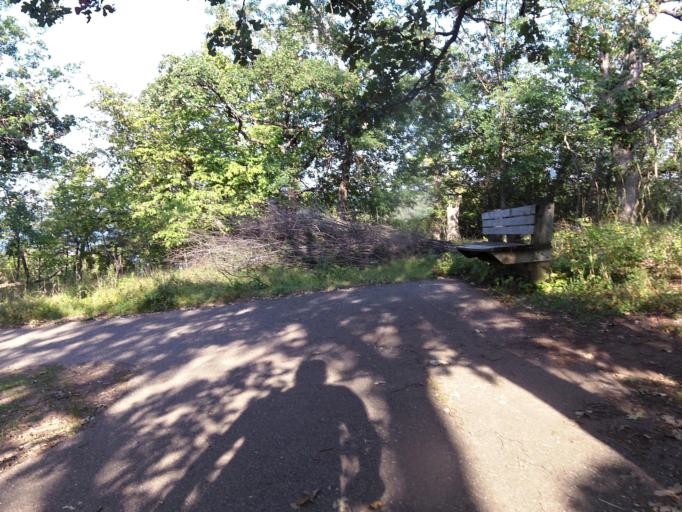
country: US
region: Minnesota
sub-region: Washington County
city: Afton
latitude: 44.8574
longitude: -92.7743
